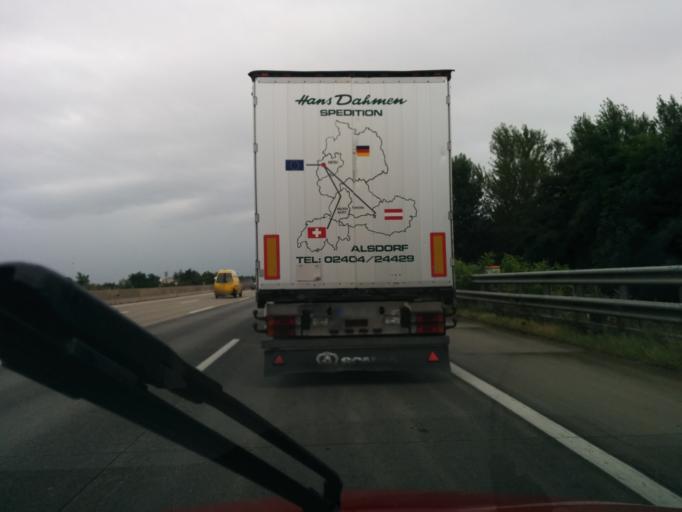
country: AT
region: Lower Austria
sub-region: Politischer Bezirk Modling
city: Guntramsdorf
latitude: 48.0429
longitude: 16.3418
